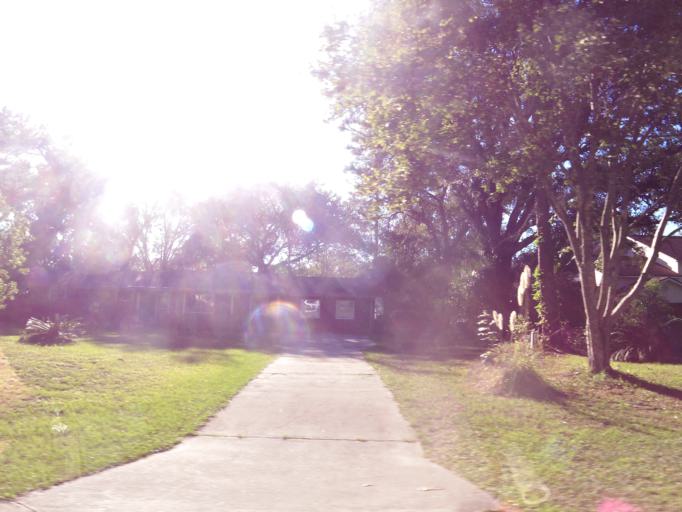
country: US
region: Florida
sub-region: Duval County
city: Atlantic Beach
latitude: 30.3265
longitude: -81.4521
